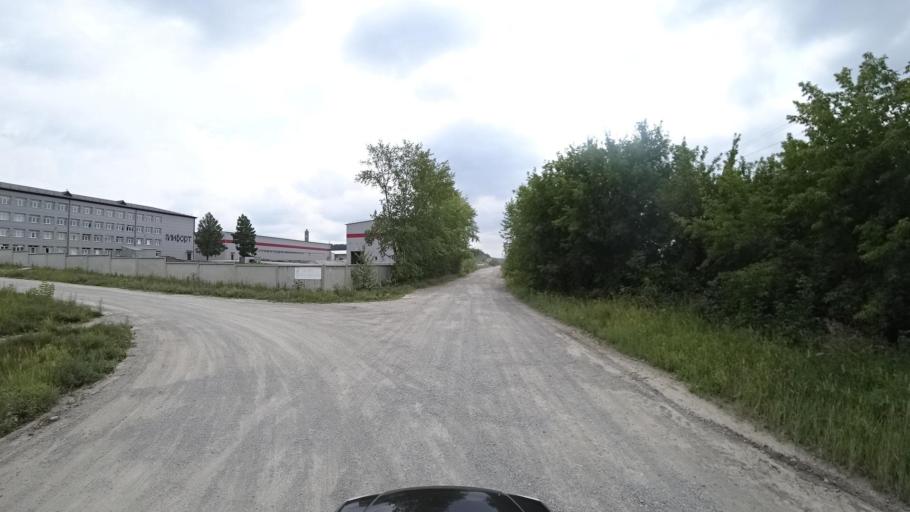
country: RU
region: Sverdlovsk
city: Kamyshlov
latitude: 56.8319
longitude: 62.7238
